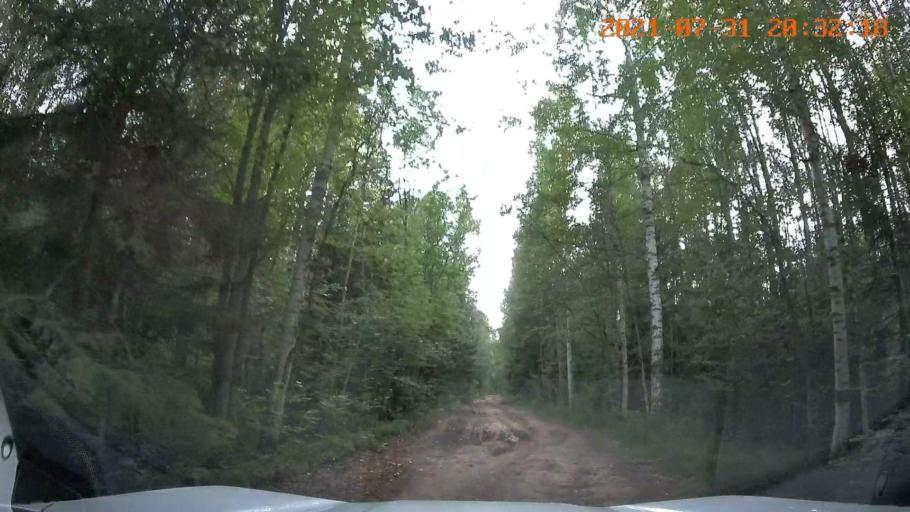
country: RU
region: Republic of Karelia
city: Pudozh
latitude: 61.6613
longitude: 36.2744
